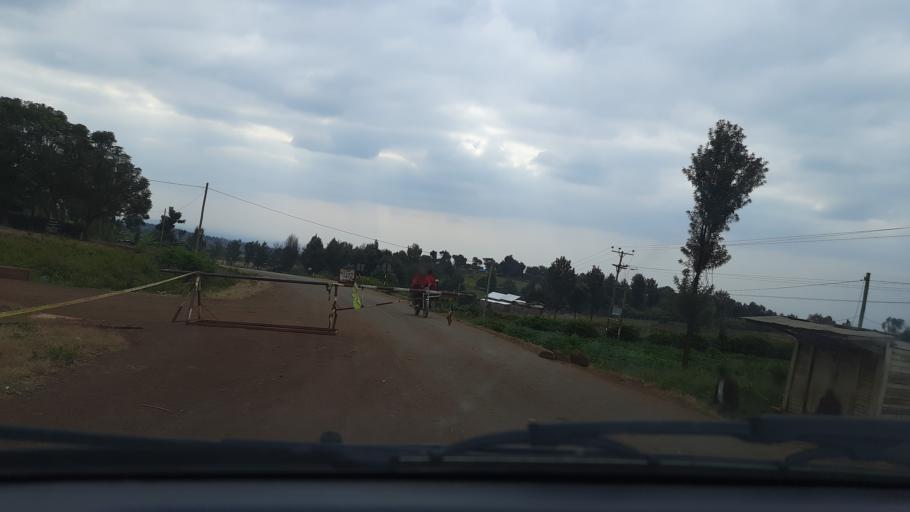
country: TZ
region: Kilimanjaro
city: Moshi
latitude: -2.8779
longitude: 37.3650
